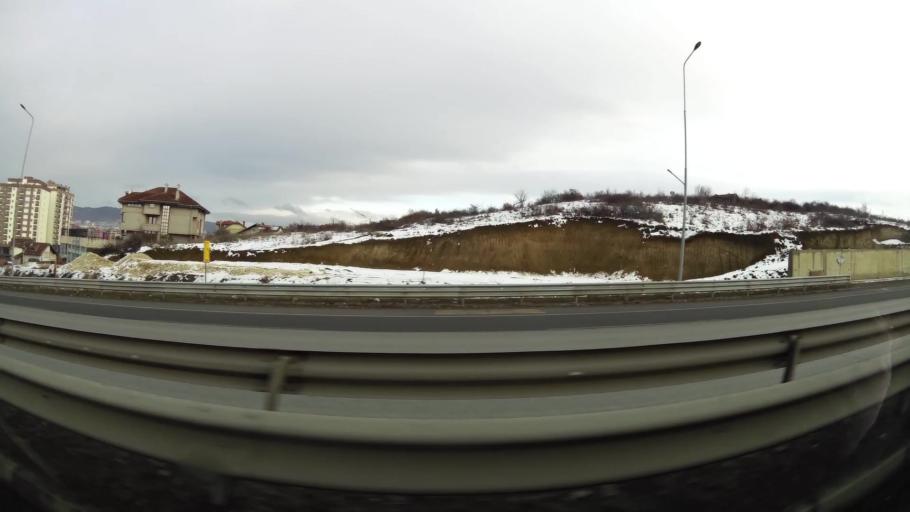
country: XK
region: Pristina
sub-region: Komuna e Prishtines
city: Pristina
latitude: 42.6390
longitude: 21.1542
